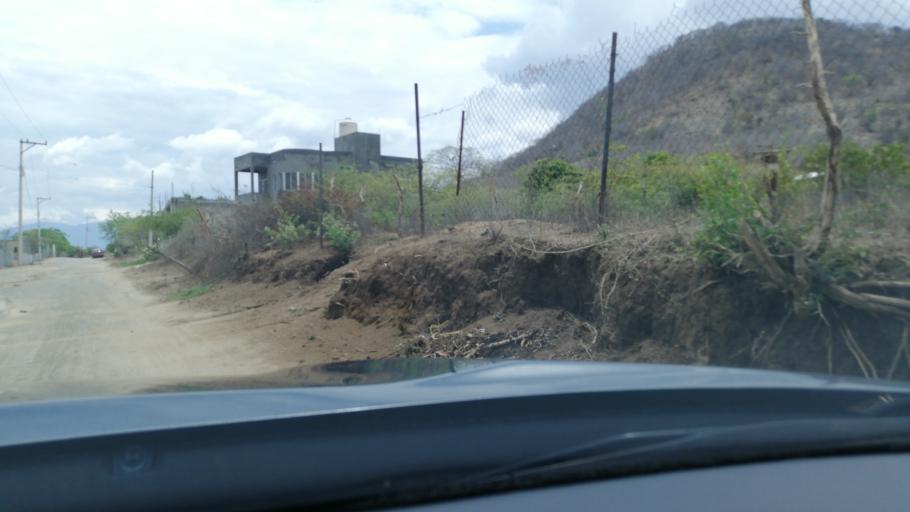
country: MX
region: Oaxaca
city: Santa Maria Jalapa del Marques
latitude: 16.4501
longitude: -95.4424
